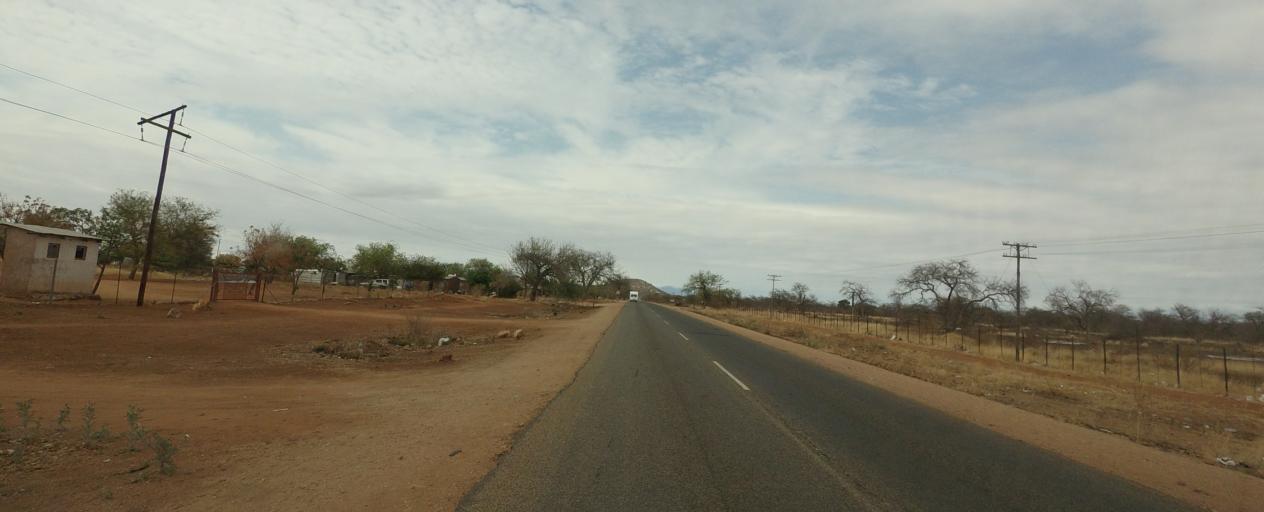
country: BW
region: Central
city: Mathathane
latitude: -22.6661
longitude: 29.1124
